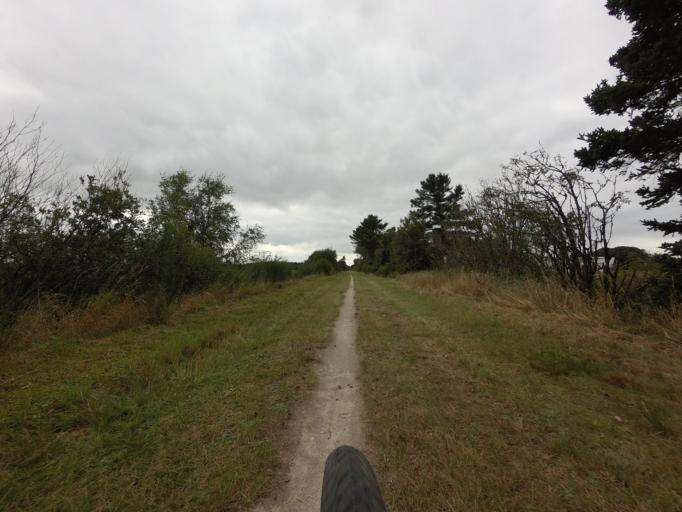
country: DK
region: Central Jutland
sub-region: Ikast-Brande Kommune
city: Brande
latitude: 55.8949
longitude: 9.0701
